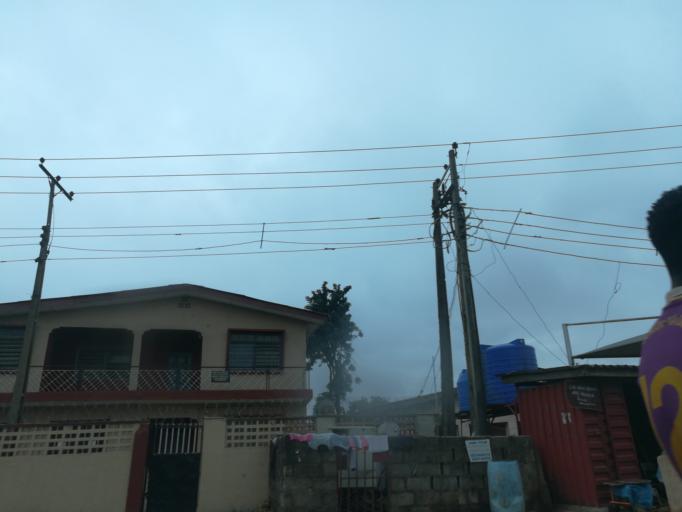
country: NG
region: Lagos
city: Oshodi
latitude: 6.5628
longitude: 3.3419
